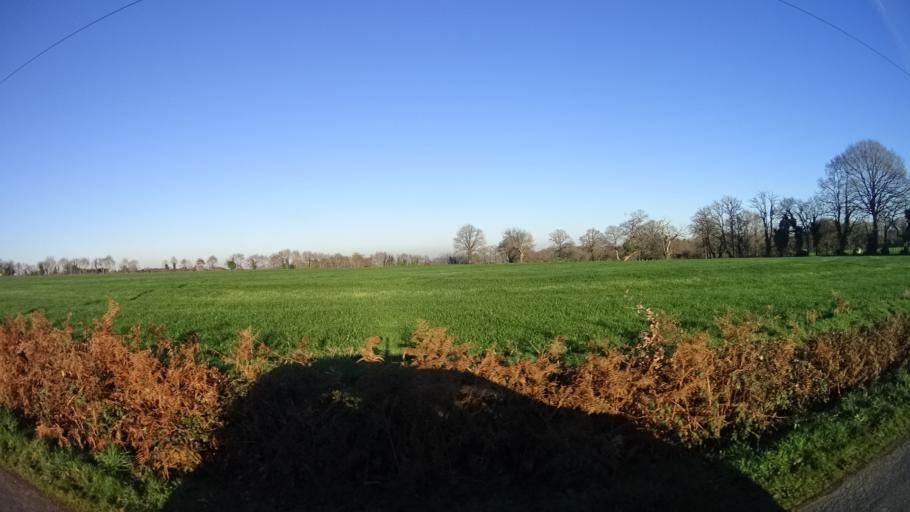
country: FR
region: Brittany
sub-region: Departement du Morbihan
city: Allaire
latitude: 47.6541
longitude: -2.1476
